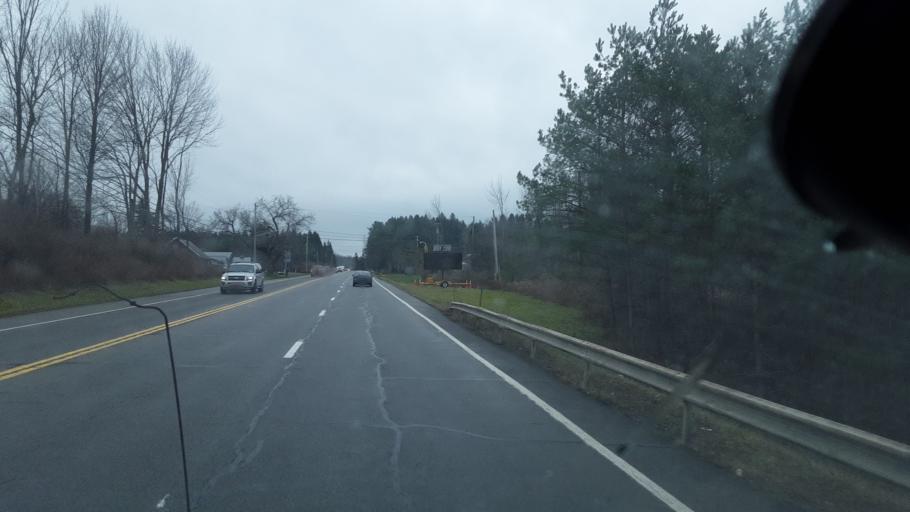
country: US
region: New York
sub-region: Erie County
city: Holland
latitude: 42.5964
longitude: -78.4970
